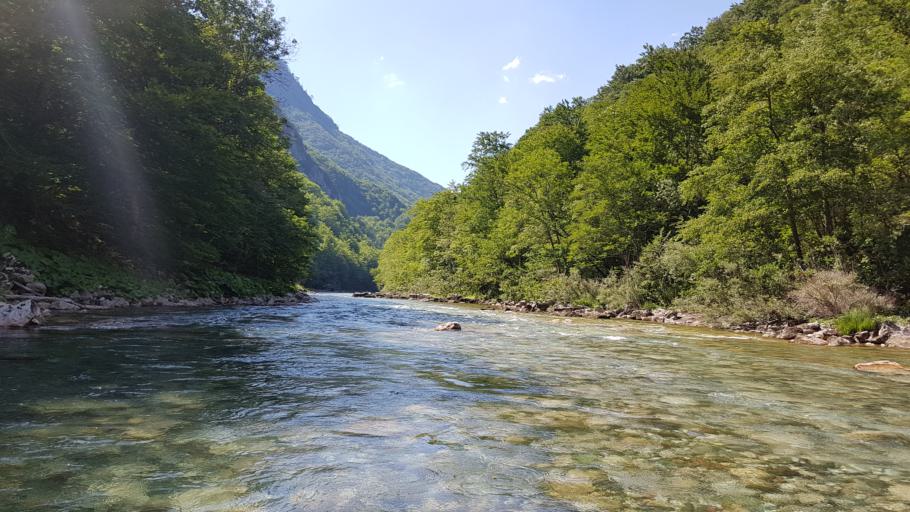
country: ME
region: Opstina Zabljak
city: Zabljak
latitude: 43.1344
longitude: 19.3081
